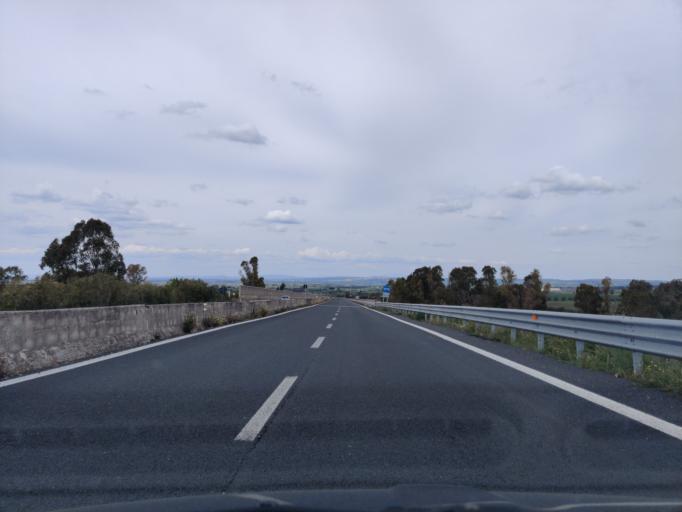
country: IT
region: Latium
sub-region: Citta metropolitana di Roma Capitale
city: Aurelia
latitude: 42.1383
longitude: 11.7947
